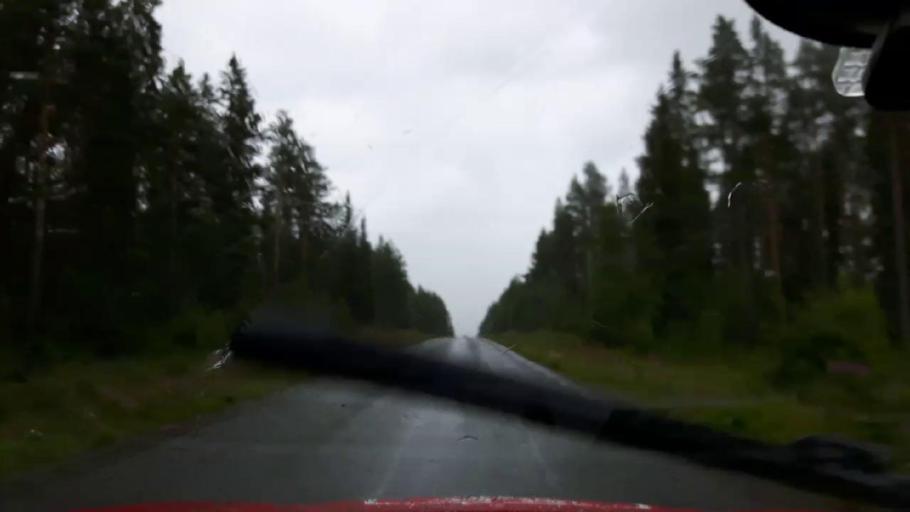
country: SE
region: Jaemtland
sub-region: OEstersunds Kommun
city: Brunflo
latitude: 62.9993
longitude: 14.7564
